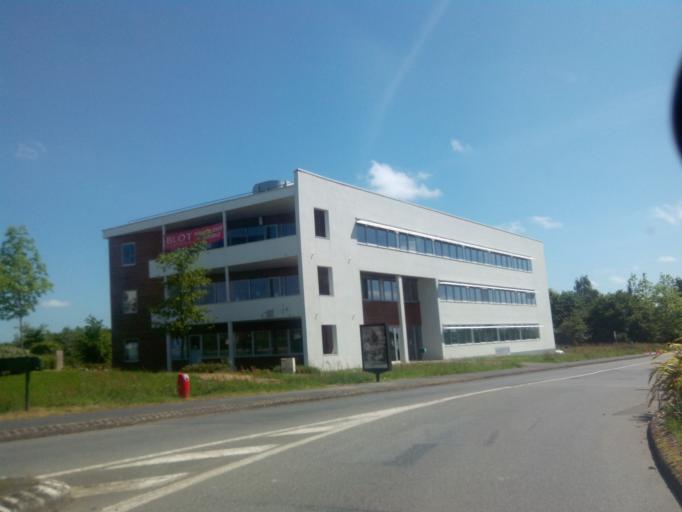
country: FR
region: Brittany
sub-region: Departement d'Ille-et-Vilaine
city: Cesson-Sevigne
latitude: 48.1316
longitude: -1.5969
